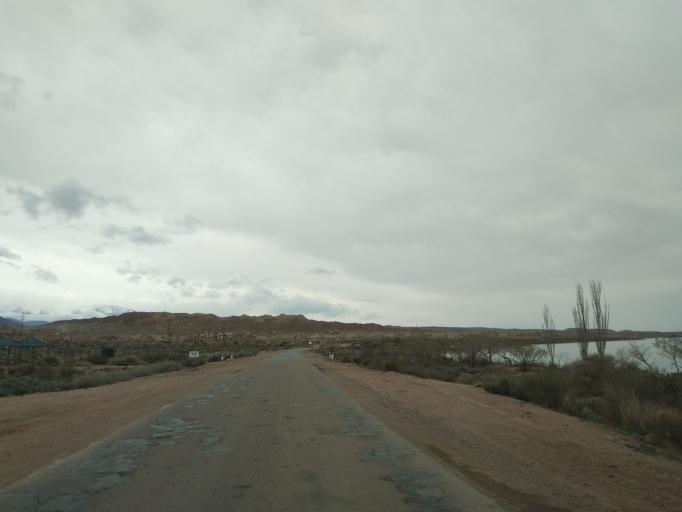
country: KG
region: Ysyk-Koel
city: Kadzhi-Say
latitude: 42.1544
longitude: 77.0954
